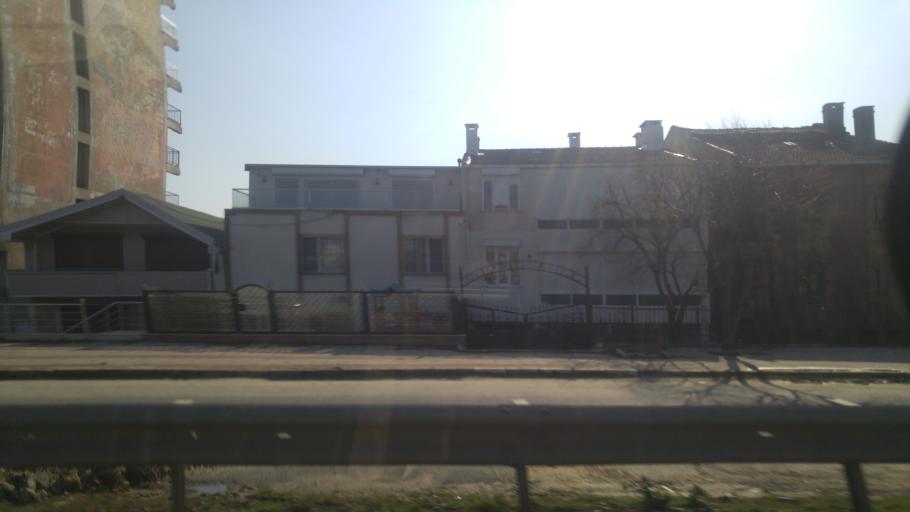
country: TR
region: Istanbul
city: Celaliye
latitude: 41.0471
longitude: 28.4019
